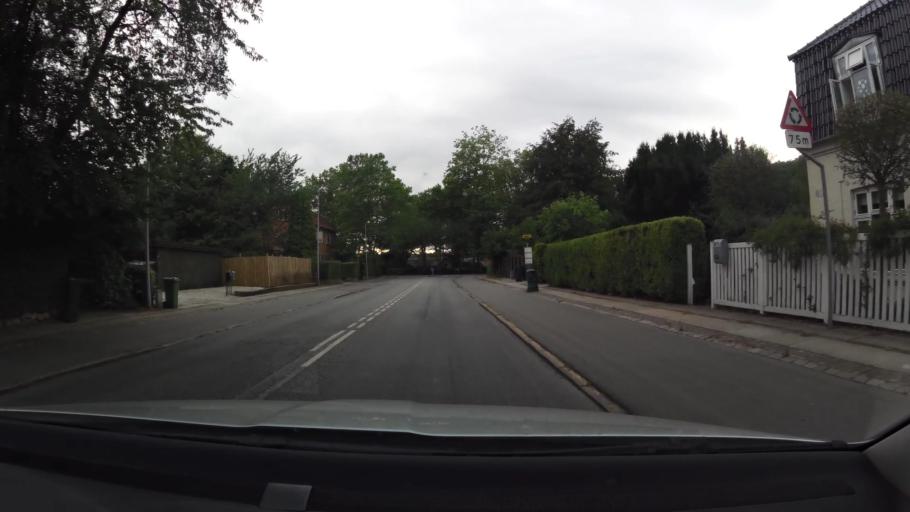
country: DK
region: Capital Region
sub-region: Lyngby-Tarbaek Kommune
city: Kongens Lyngby
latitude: 55.7976
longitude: 12.5159
